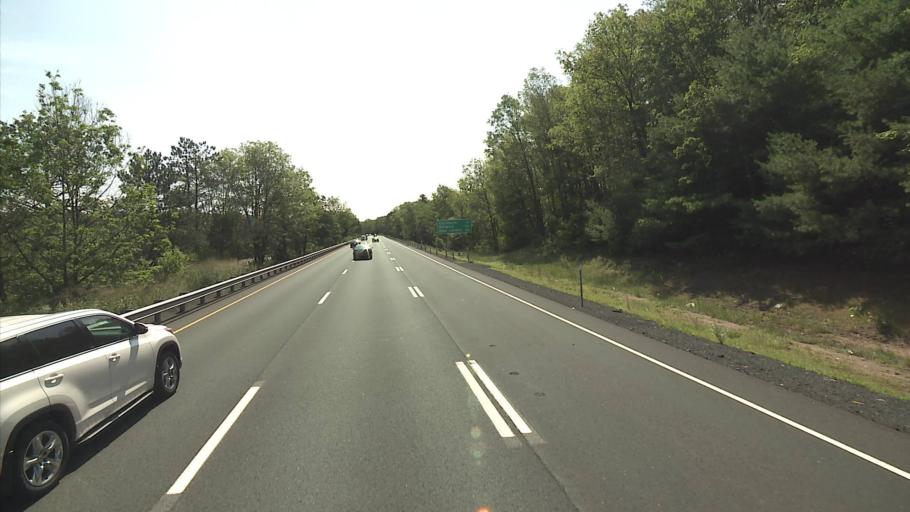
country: US
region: Connecticut
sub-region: Hartford County
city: Terramuggus
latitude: 41.6609
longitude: -72.5204
